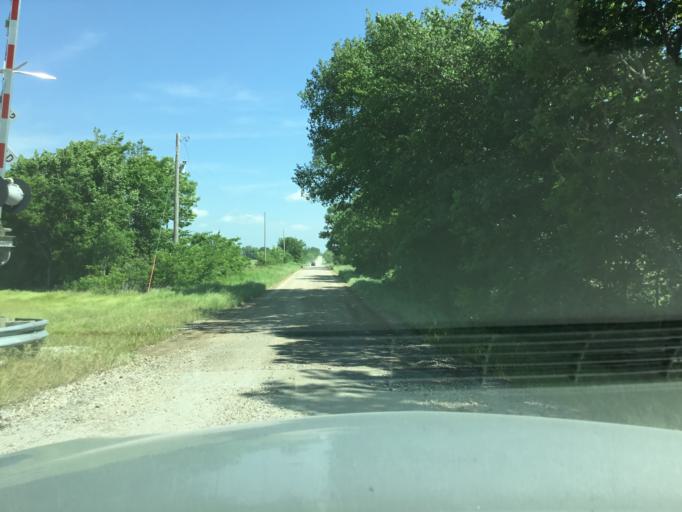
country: US
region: Kansas
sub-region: Labette County
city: Oswego
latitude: 37.1889
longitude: -95.1400
